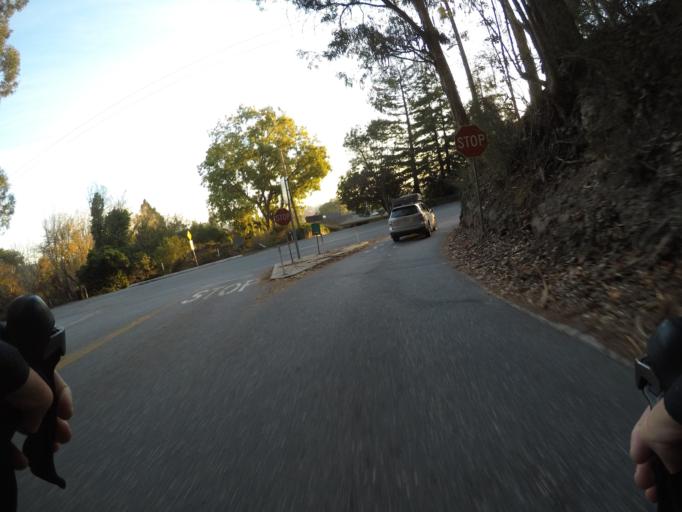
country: US
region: California
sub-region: Santa Cruz County
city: Pasatiempo
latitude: 36.9919
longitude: -122.0080
